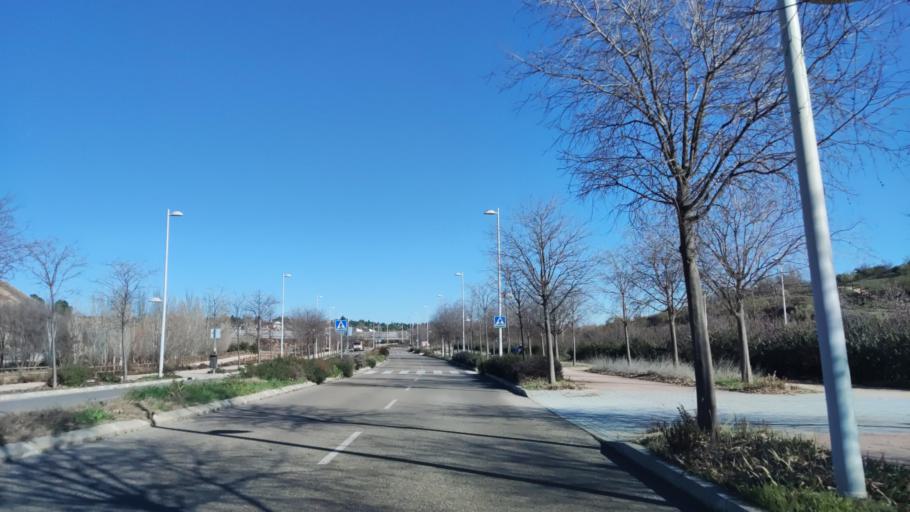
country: ES
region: Madrid
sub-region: Provincia de Madrid
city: Hortaleza
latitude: 40.4962
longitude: -3.6379
